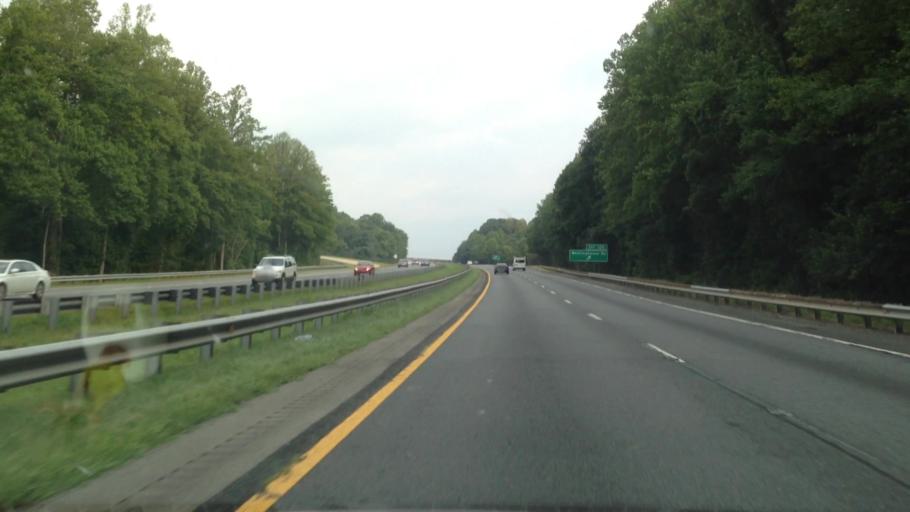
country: US
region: North Carolina
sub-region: Forsyth County
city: Rural Hall
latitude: 36.2253
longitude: -80.3178
